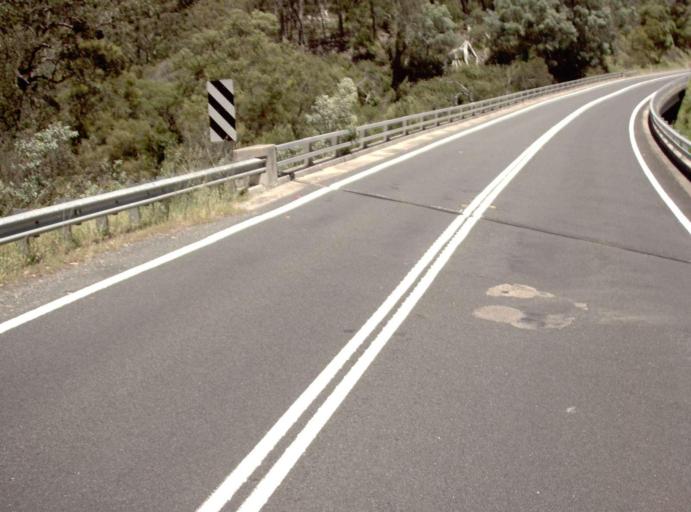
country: AU
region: Victoria
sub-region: East Gippsland
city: Lakes Entrance
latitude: -37.8018
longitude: 148.0476
